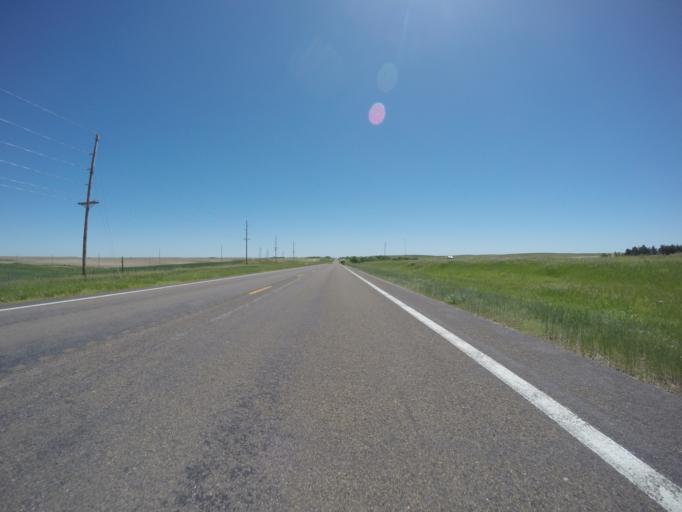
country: US
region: Kansas
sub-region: Norton County
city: Norton
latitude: 39.8285
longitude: -99.6114
